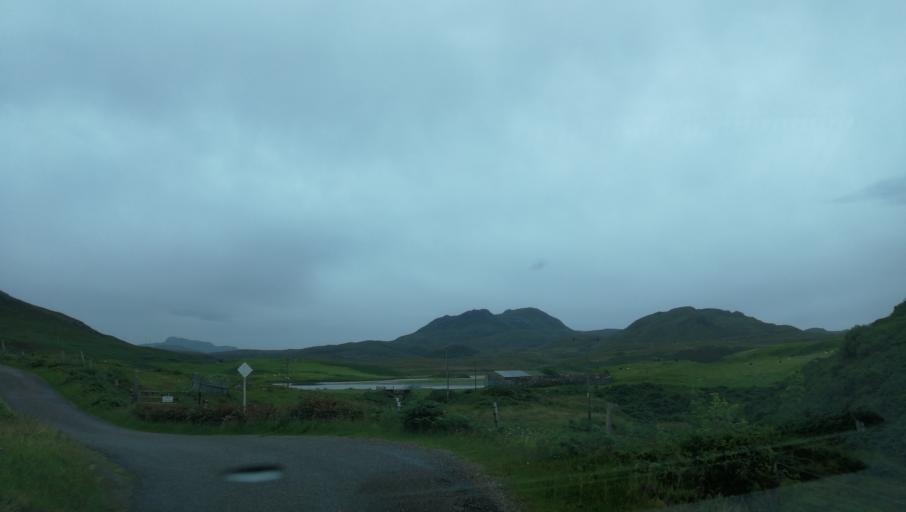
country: GB
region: Scotland
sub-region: Argyll and Bute
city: Isle Of Mull
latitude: 56.7245
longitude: -6.2045
